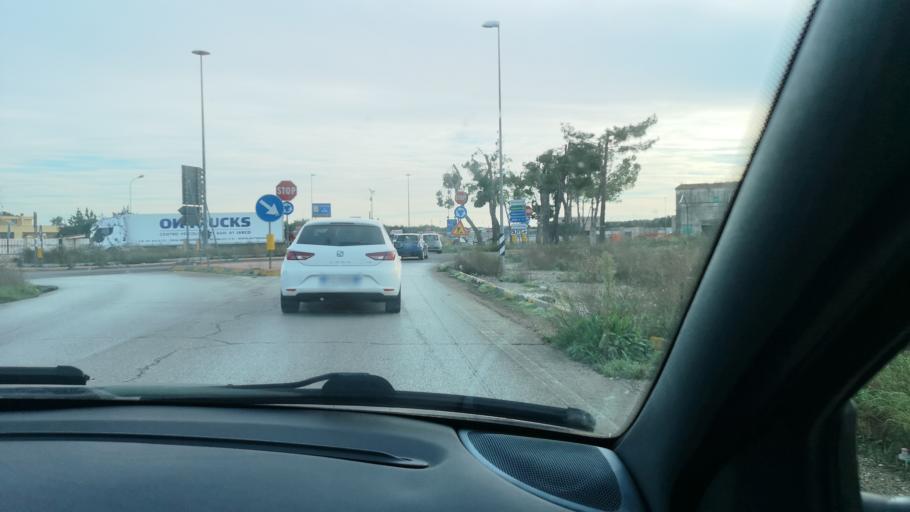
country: IT
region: Apulia
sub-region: Provincia di Bari
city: Sannicandro di Bari
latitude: 40.9915
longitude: 16.7993
